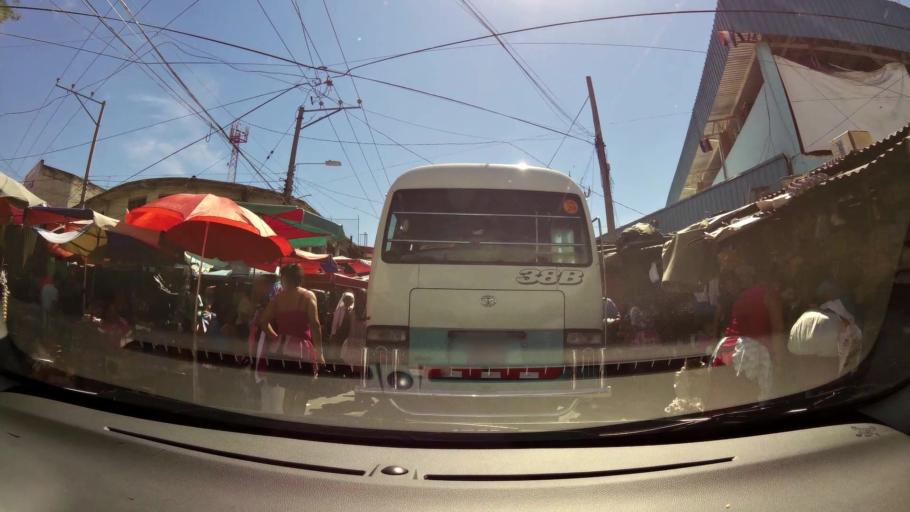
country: SV
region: San Salvador
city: Apopa
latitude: 13.8006
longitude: -89.1788
